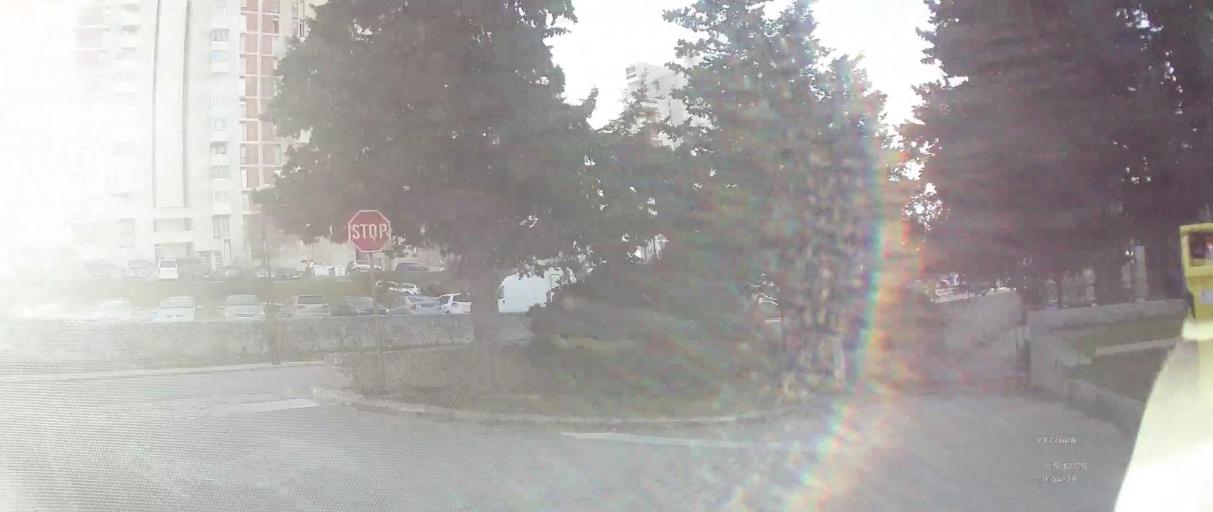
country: HR
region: Splitsko-Dalmatinska
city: Vranjic
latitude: 43.5067
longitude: 16.4732
